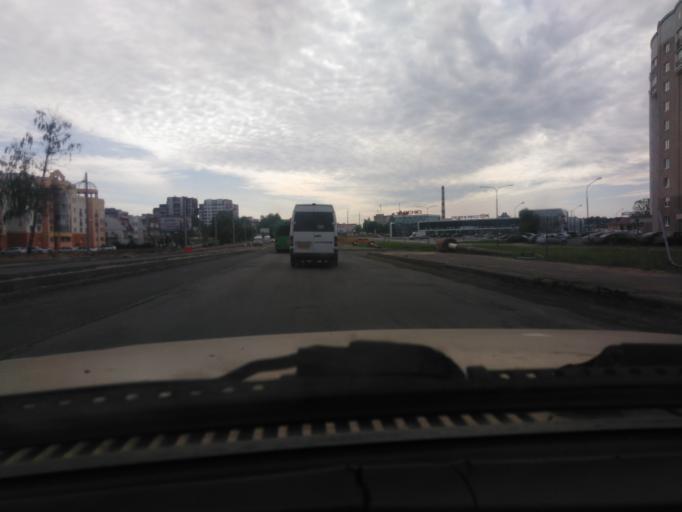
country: BY
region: Mogilev
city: Mahilyow
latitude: 53.9193
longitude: 30.2968
